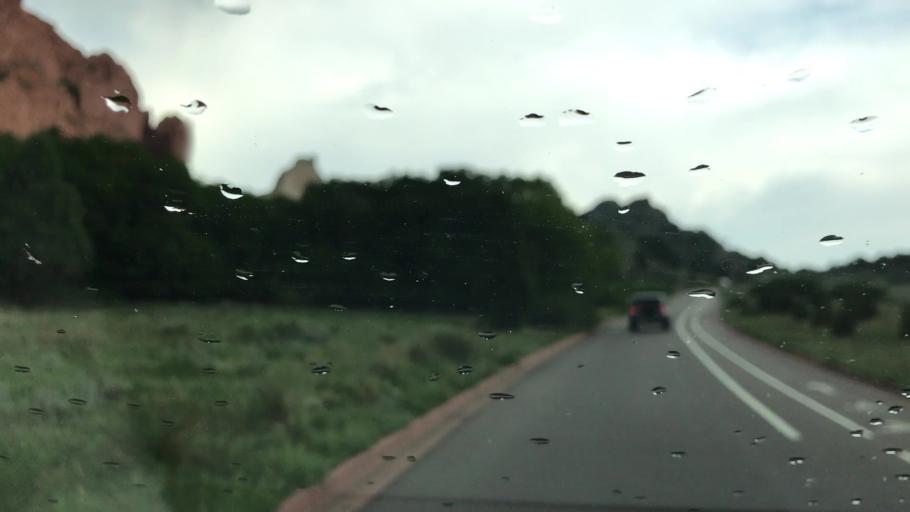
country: US
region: Colorado
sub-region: El Paso County
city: Manitou Springs
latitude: 38.8774
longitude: -104.8780
